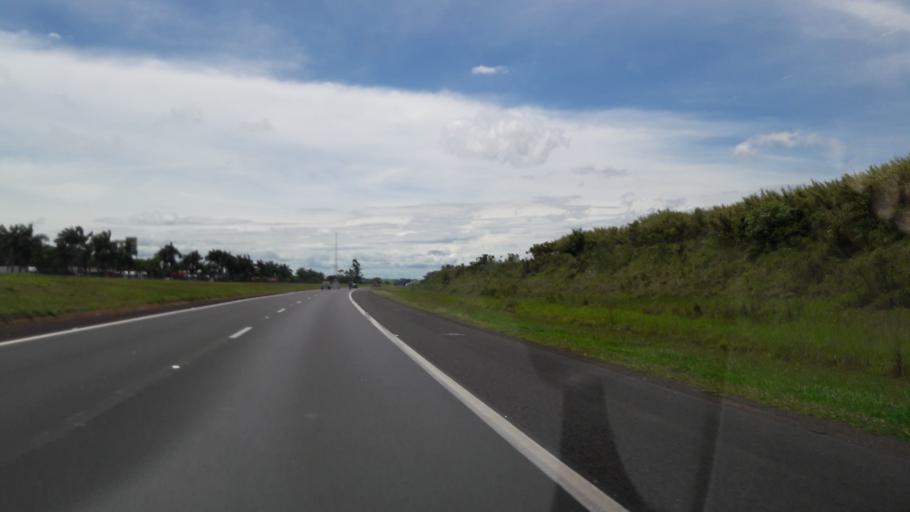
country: BR
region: Sao Paulo
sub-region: Avare
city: Avare
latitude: -22.9568
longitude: -48.8612
